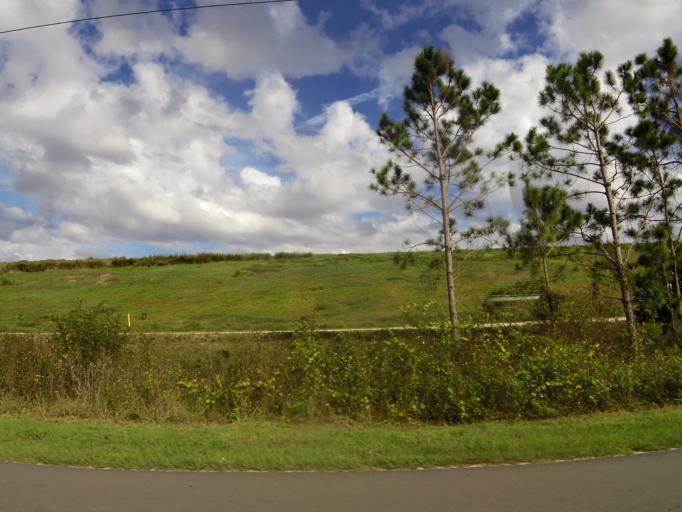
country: US
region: Florida
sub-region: Saint Johns County
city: Villano Beach
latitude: 29.9990
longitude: -81.3963
